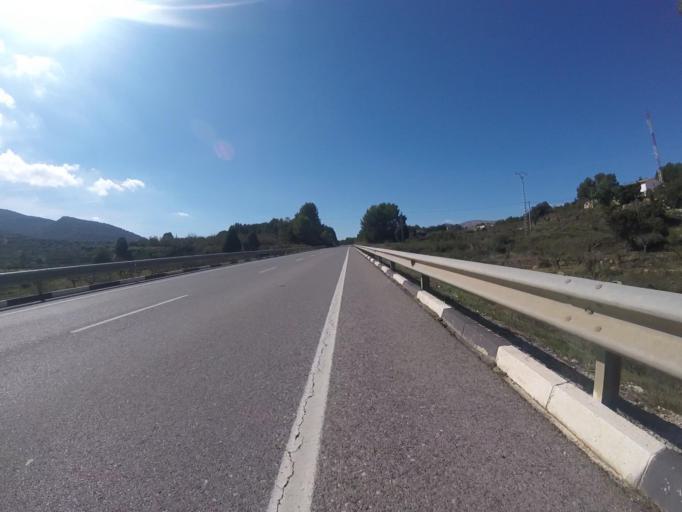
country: ES
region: Valencia
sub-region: Provincia de Castello
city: Sierra-Engarceran
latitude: 40.3222
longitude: -0.0245
